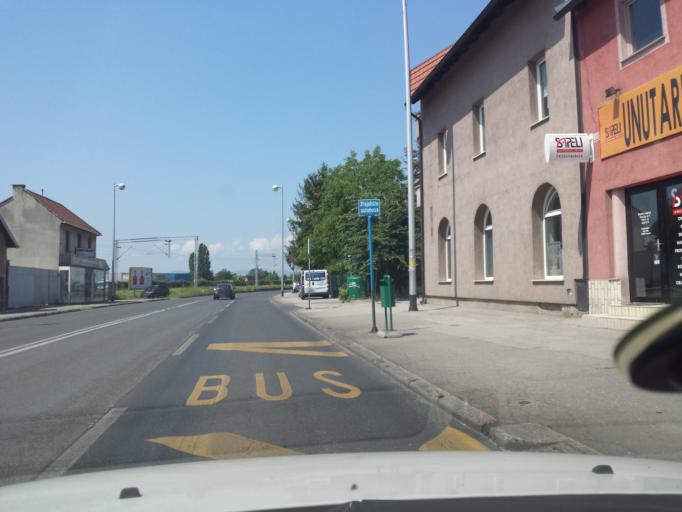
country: HR
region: Grad Zagreb
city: Jankomir
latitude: 45.8116
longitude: 15.9174
